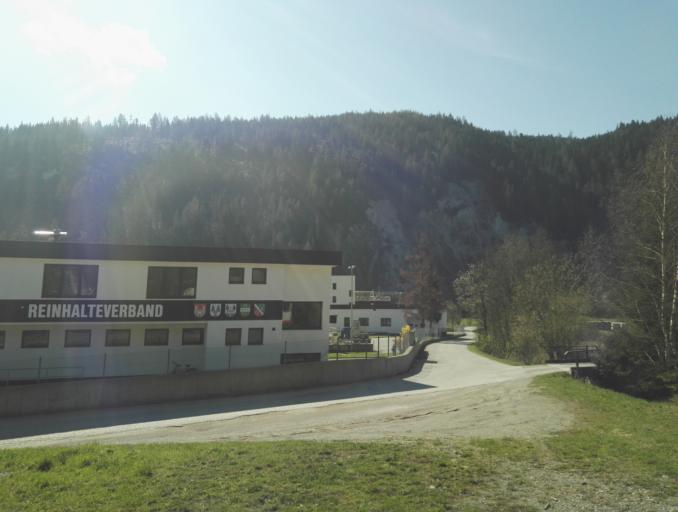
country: AT
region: Salzburg
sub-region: Politischer Bezirk Sankt Johann im Pongau
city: Forstau
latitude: 47.3879
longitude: 13.4954
